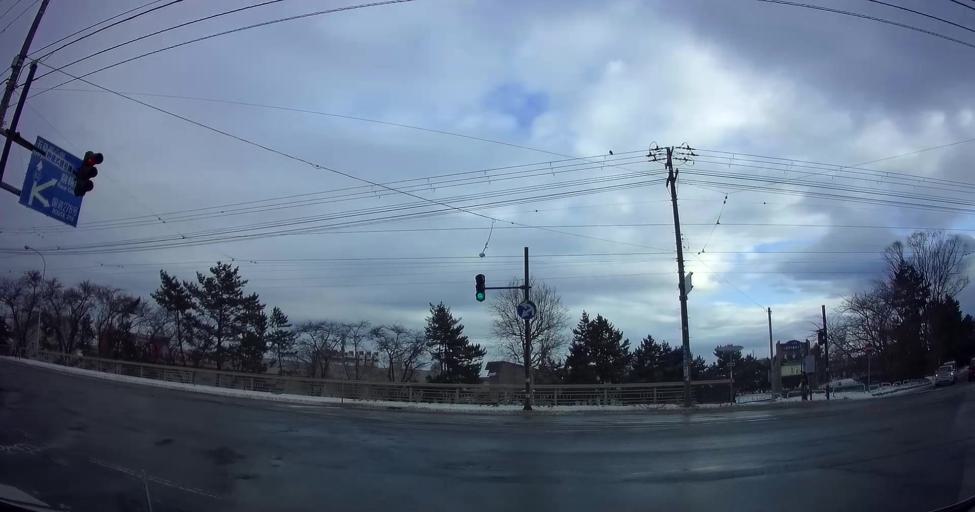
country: JP
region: Hokkaido
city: Hakodate
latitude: 41.7773
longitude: 140.7397
